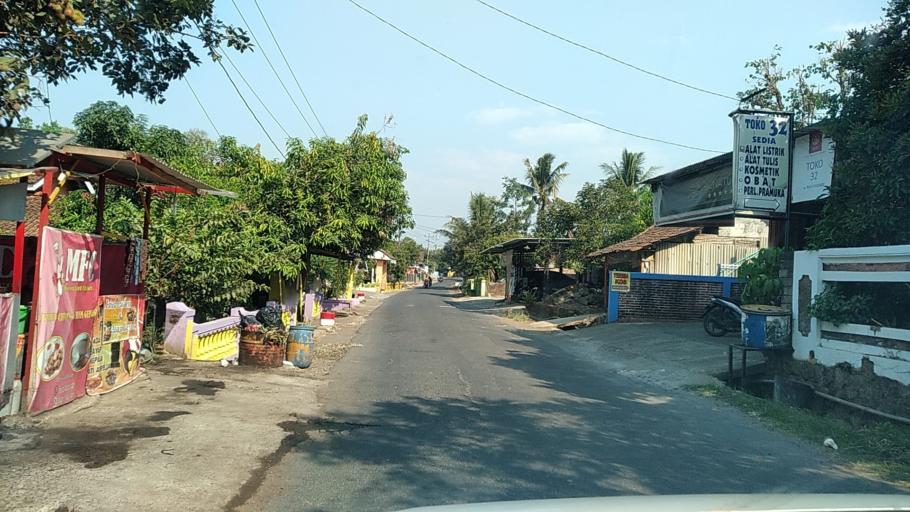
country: ID
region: Central Java
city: Semarang
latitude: -7.0514
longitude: 110.3269
